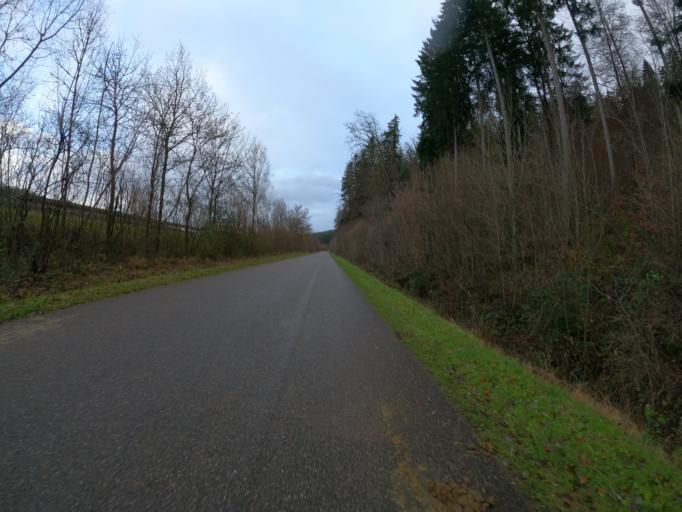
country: DE
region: Baden-Wuerttemberg
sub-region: Regierungsbezirk Stuttgart
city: Lorch
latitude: 48.7915
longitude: 9.7185
